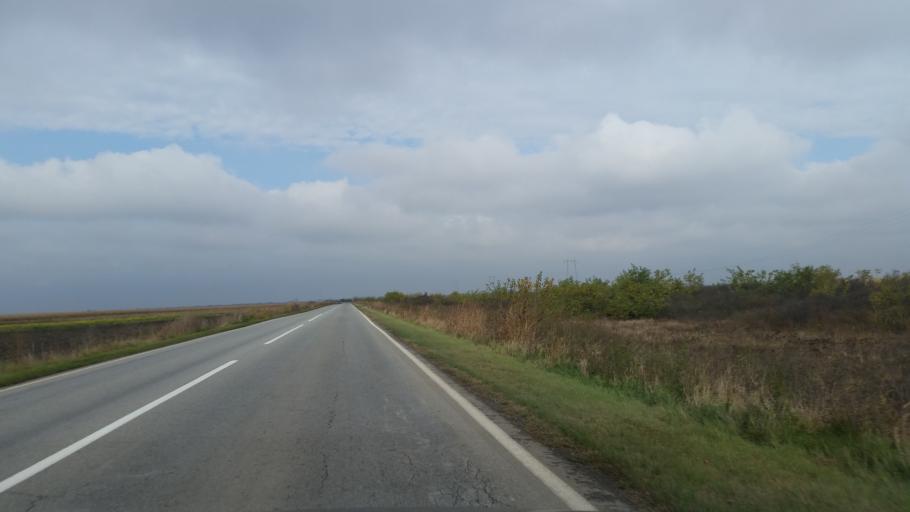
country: RS
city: Melenci
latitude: 45.4765
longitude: 20.3389
